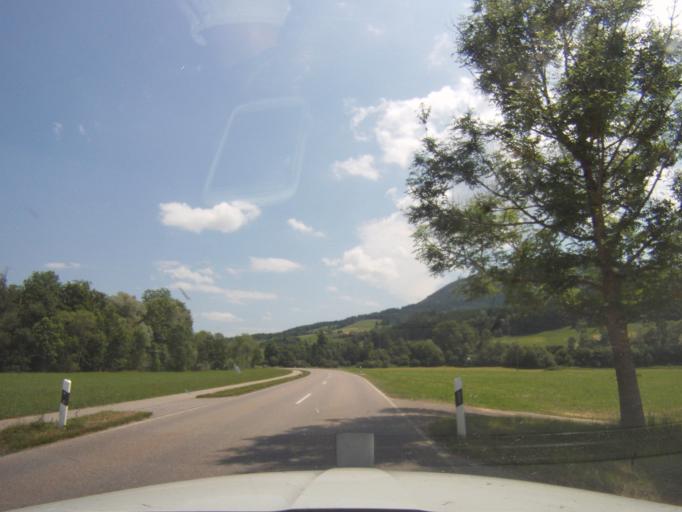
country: DE
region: Bavaria
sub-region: Swabia
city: Wertach
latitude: 47.6027
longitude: 10.4280
